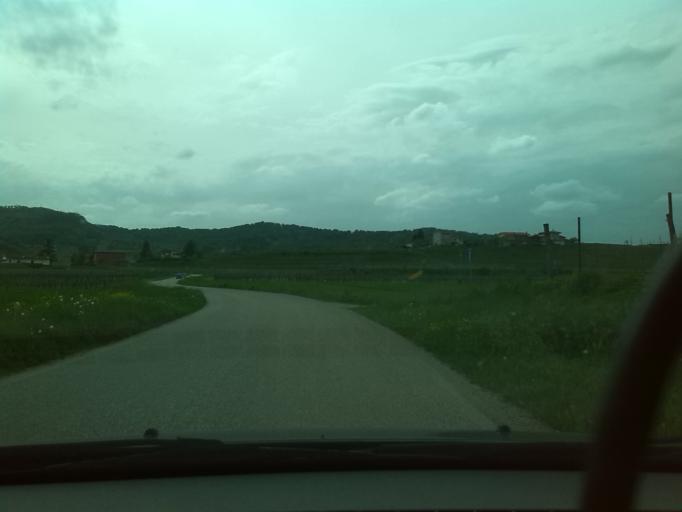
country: SI
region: Brda
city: Dobrovo
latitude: 45.9750
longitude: 13.5092
